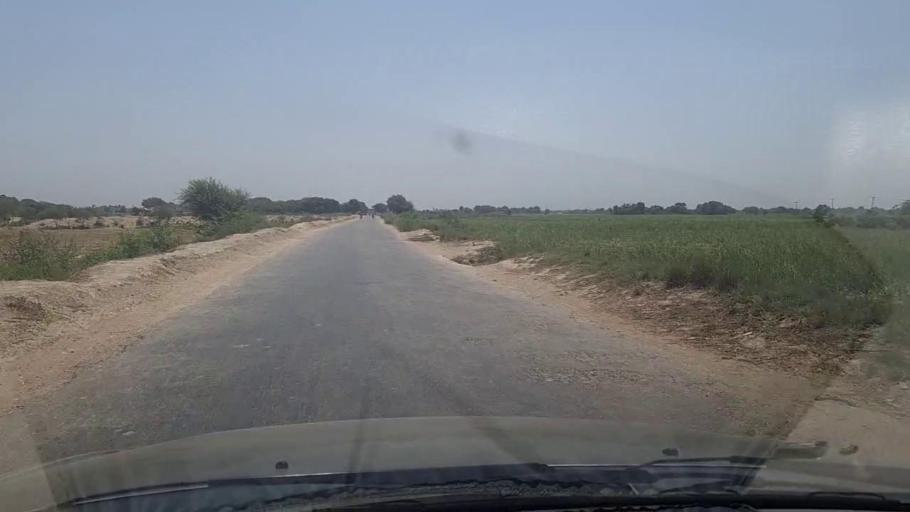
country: PK
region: Sindh
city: Chambar
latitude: 25.2693
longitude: 68.6372
